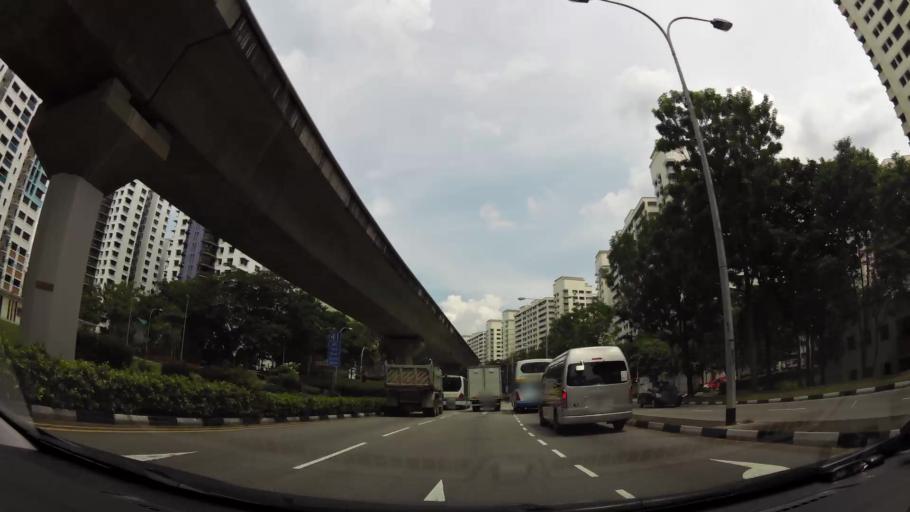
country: MY
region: Johor
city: Johor Bahru
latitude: 1.3857
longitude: 103.7632
